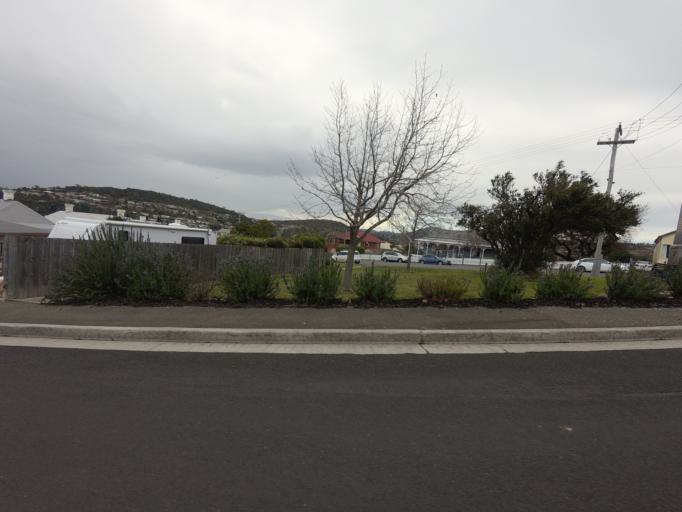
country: AU
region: Tasmania
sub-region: Clarence
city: Bellerive
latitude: -42.8773
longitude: 147.3655
